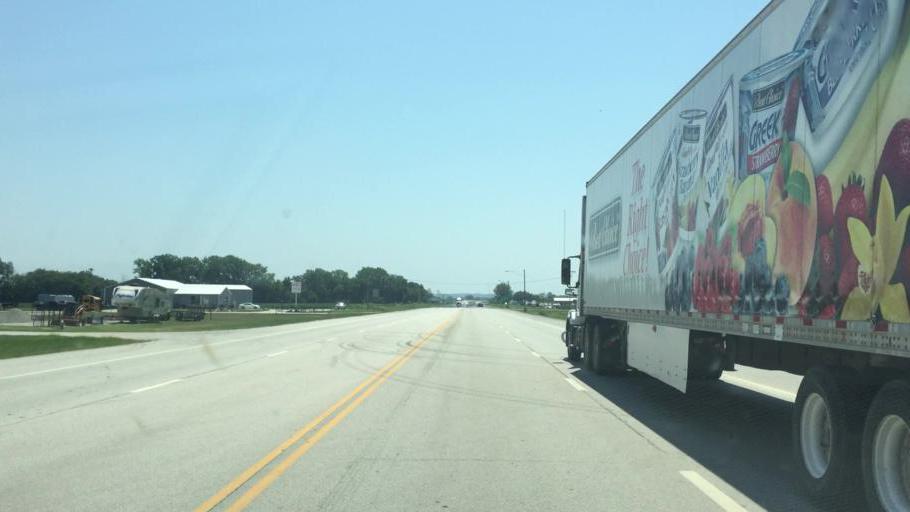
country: US
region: Kansas
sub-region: Doniphan County
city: Wathena
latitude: 39.7583
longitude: -94.9427
